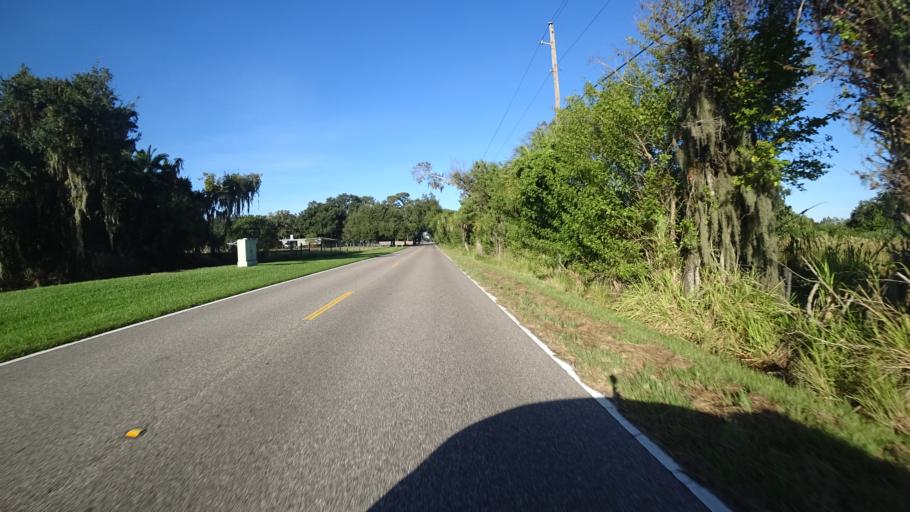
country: US
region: Florida
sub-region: Manatee County
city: Memphis
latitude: 27.5682
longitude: -82.5423
